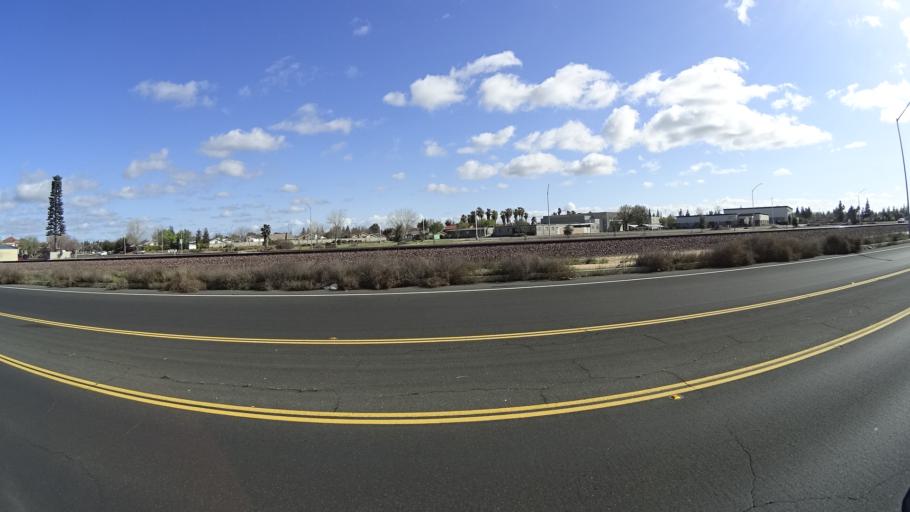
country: US
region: California
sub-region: Fresno County
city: West Park
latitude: 36.8319
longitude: -119.8785
